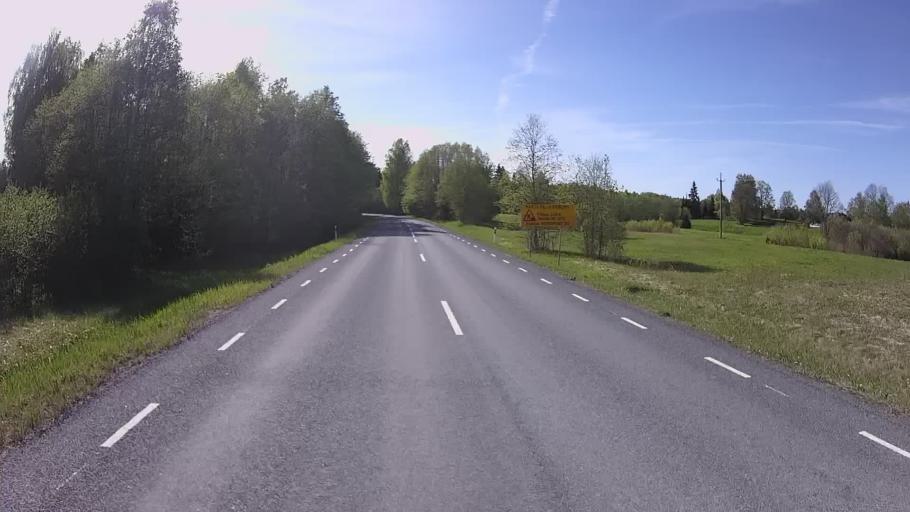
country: EE
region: Vorumaa
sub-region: Antsla vald
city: Vana-Antsla
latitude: 57.9489
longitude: 26.4058
